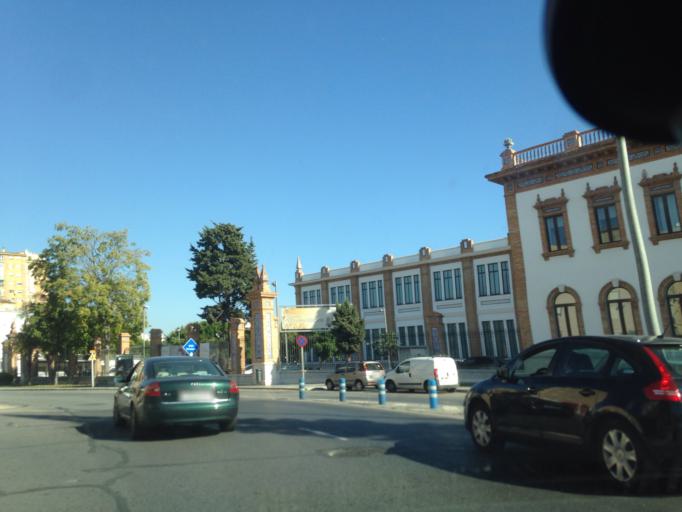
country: ES
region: Andalusia
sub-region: Provincia de Malaga
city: Malaga
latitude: 36.6999
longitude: -4.4398
